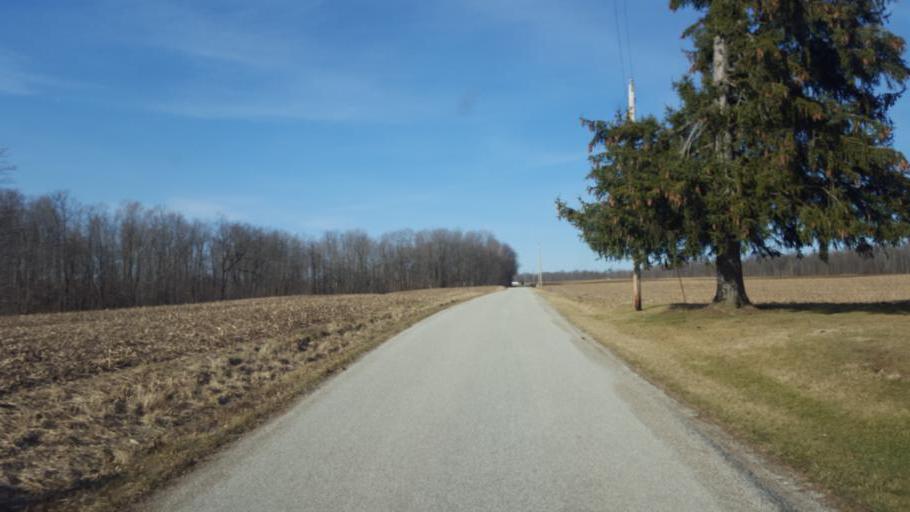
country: US
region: Ohio
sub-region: Morrow County
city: Mount Gilead
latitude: 40.5834
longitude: -82.7008
